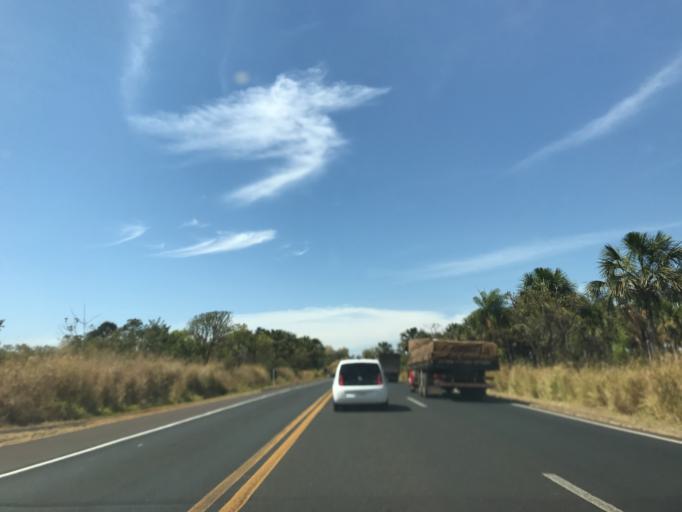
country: BR
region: Minas Gerais
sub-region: Prata
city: Prata
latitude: -19.0891
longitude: -48.9909
